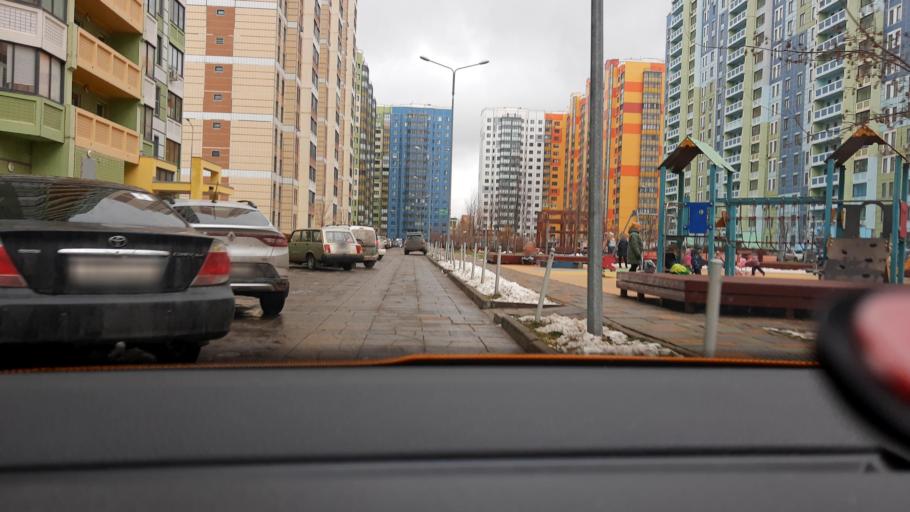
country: RU
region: Moscow
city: Businovo
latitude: 55.8783
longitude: 37.5068
